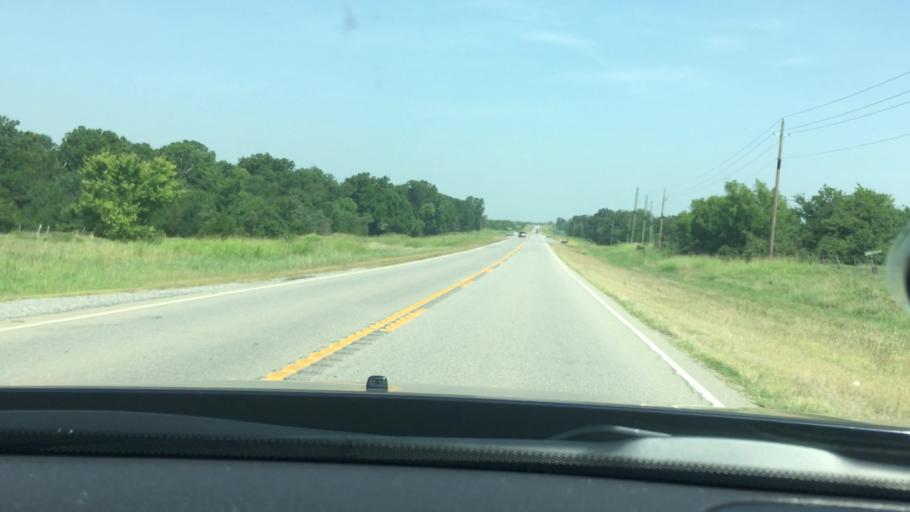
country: US
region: Oklahoma
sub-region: Atoka County
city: Atoka
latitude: 34.4426
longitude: -96.2050
